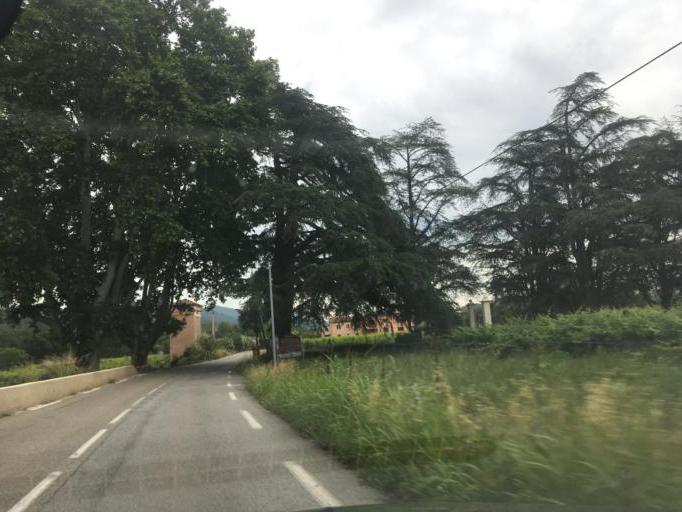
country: FR
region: Provence-Alpes-Cote d'Azur
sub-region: Departement du Var
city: Pierrefeu-du-Var
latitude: 43.2331
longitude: 6.1878
